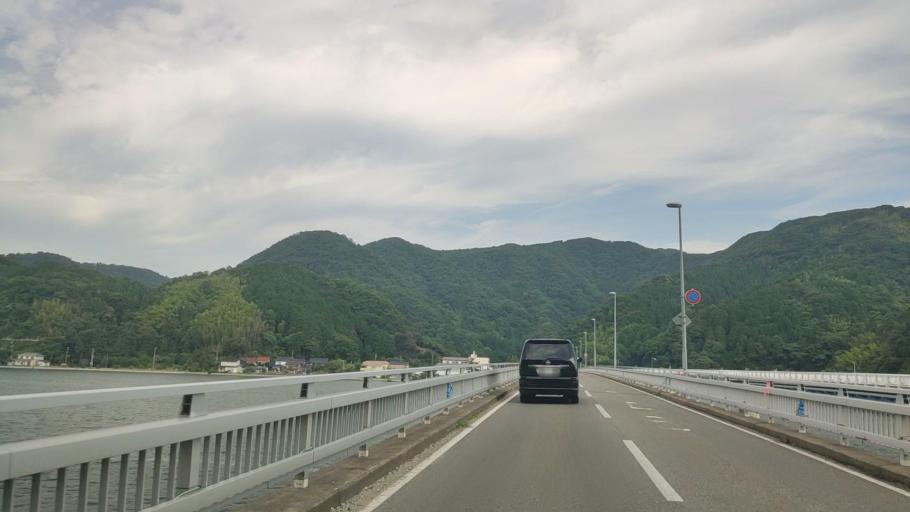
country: JP
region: Hyogo
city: Toyooka
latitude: 35.6409
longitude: 134.8280
